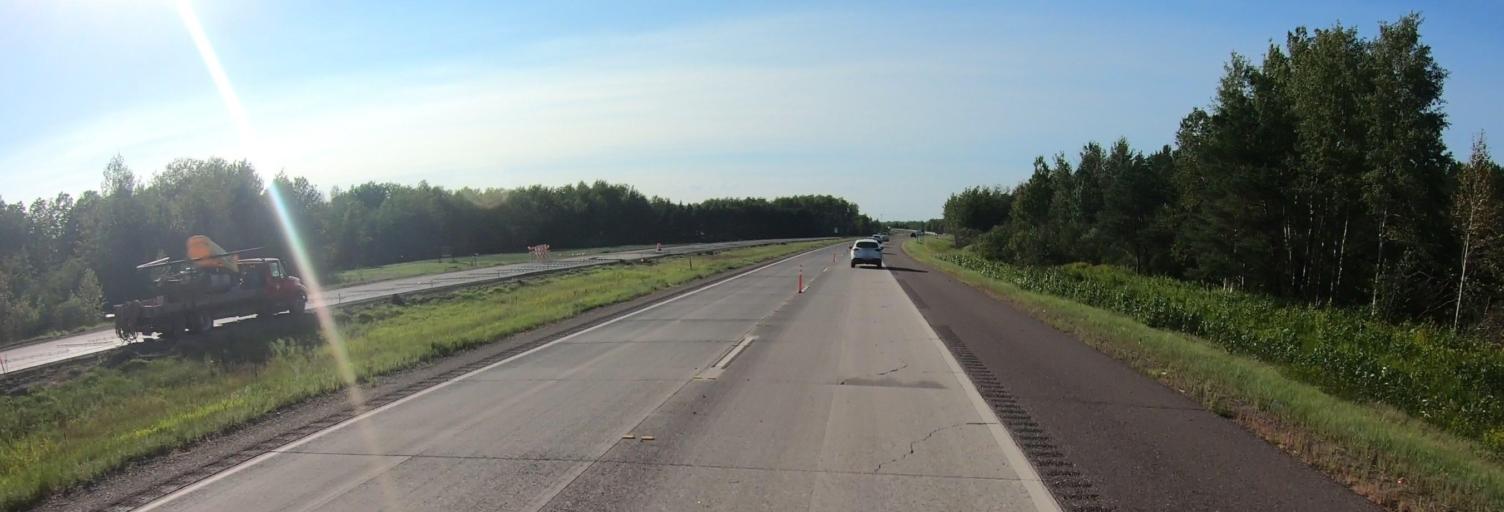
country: US
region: Minnesota
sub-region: Saint Louis County
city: Hermantown
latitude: 46.8721
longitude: -92.3378
